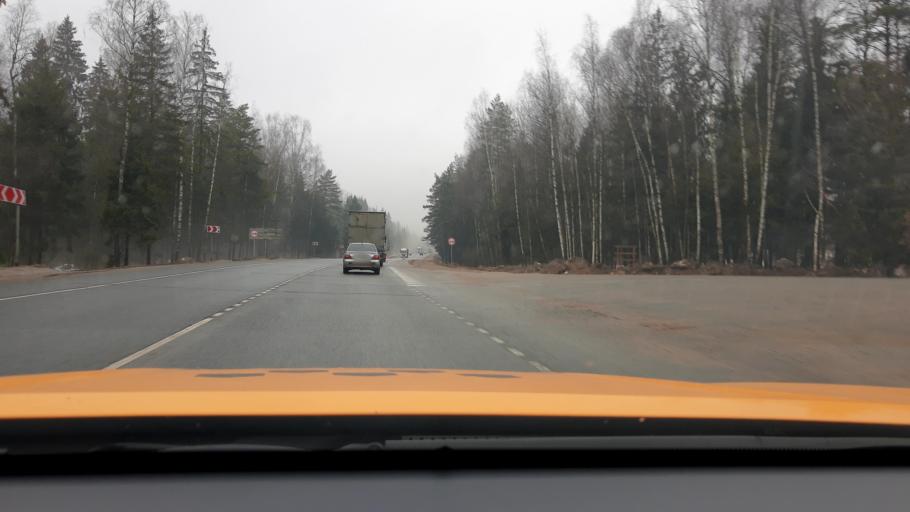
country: RU
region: Moskovskaya
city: Zelenogradskiy
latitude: 56.0838
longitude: 38.0022
